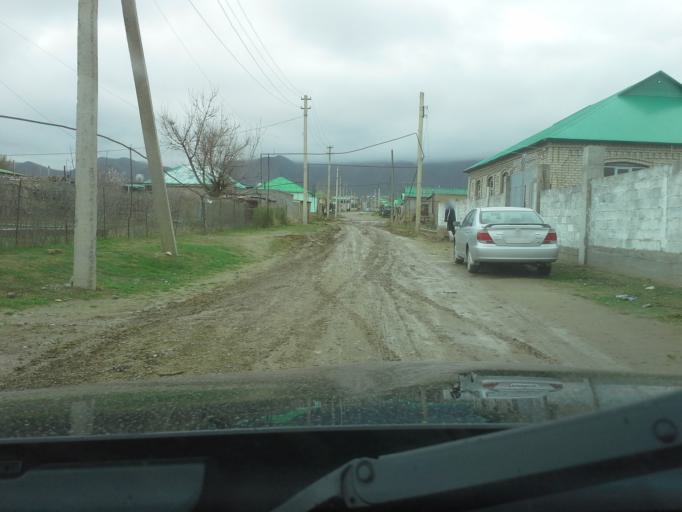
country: TM
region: Ahal
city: Abadan
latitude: 37.9681
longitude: 58.2096
